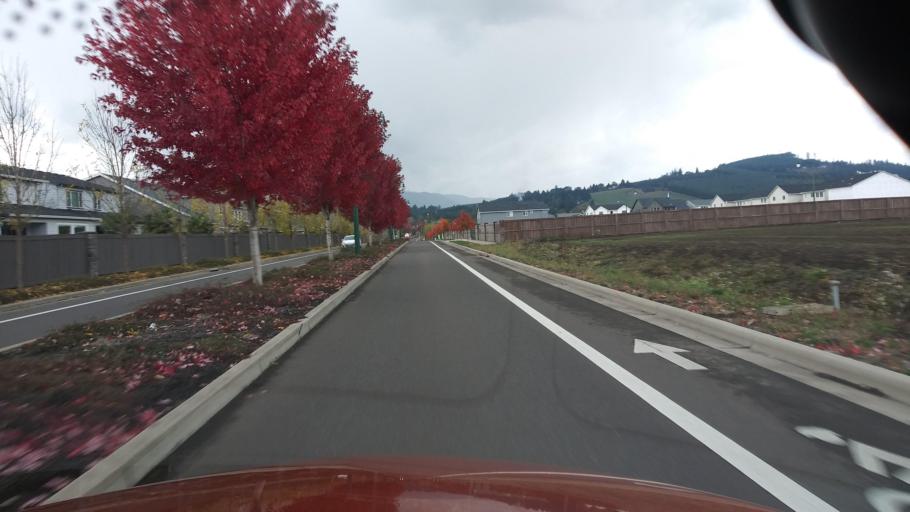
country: US
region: Oregon
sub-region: Washington County
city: Forest Grove
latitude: 45.5391
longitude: -123.1173
